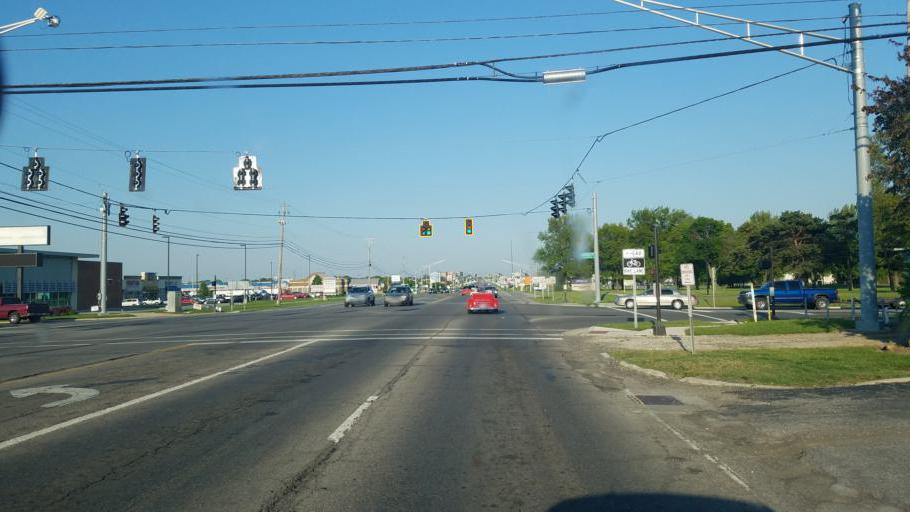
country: US
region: Ohio
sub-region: Marion County
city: Marion
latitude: 40.5809
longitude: -83.0933
